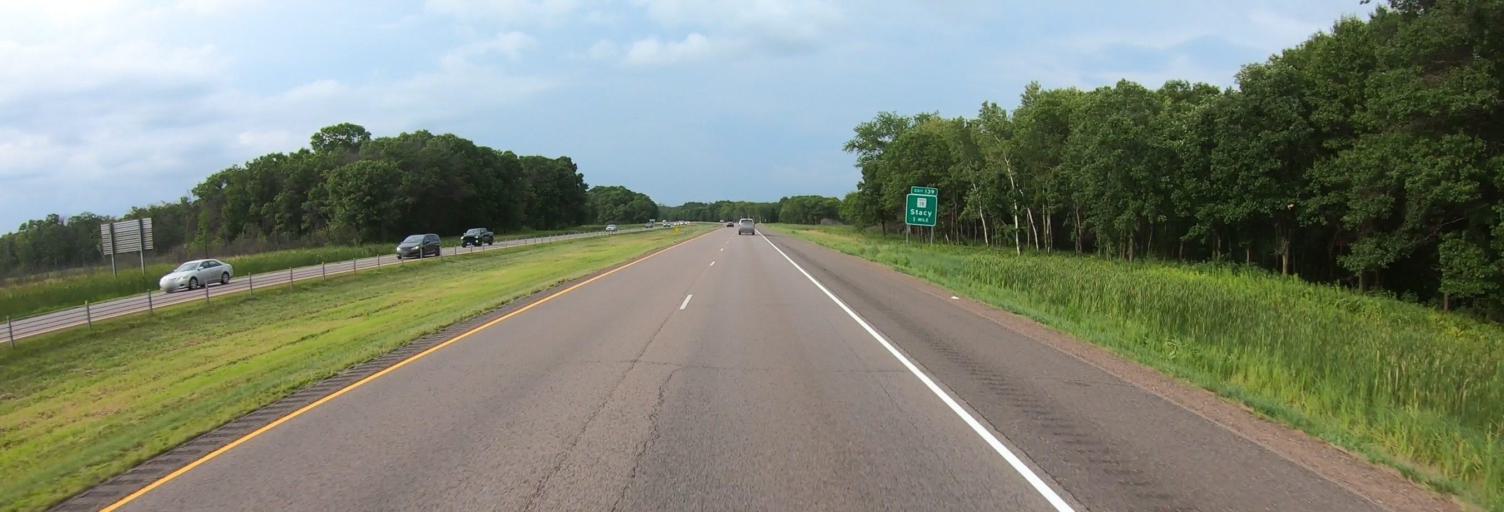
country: US
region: Minnesota
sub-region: Chisago County
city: Stacy
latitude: 45.3808
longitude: -92.9921
